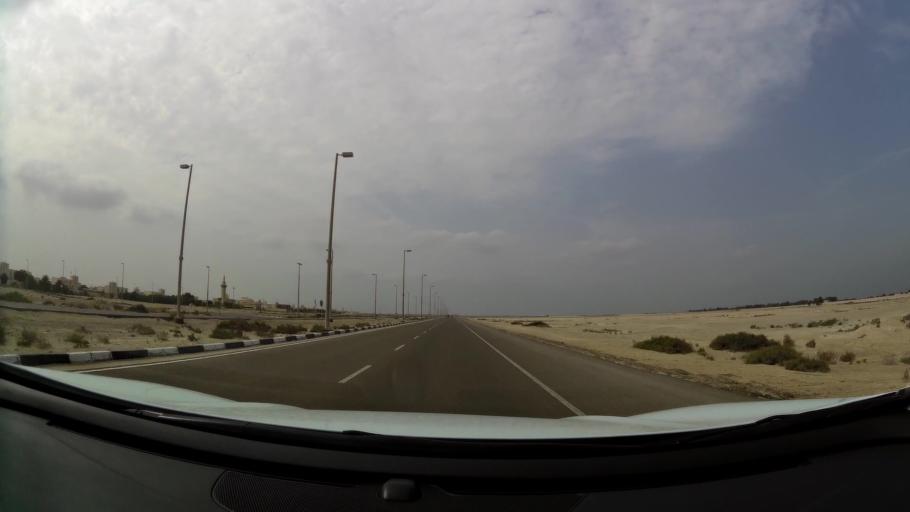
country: AE
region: Abu Dhabi
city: Abu Dhabi
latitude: 24.6476
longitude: 54.6722
